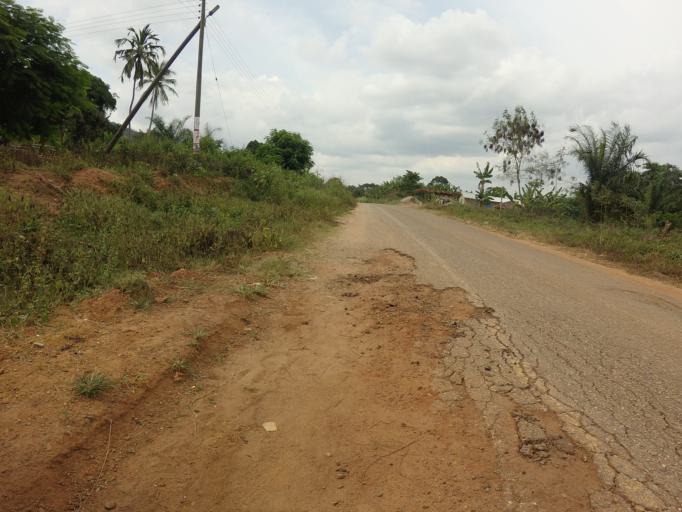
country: GH
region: Volta
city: Ho
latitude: 6.6238
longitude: 0.3295
